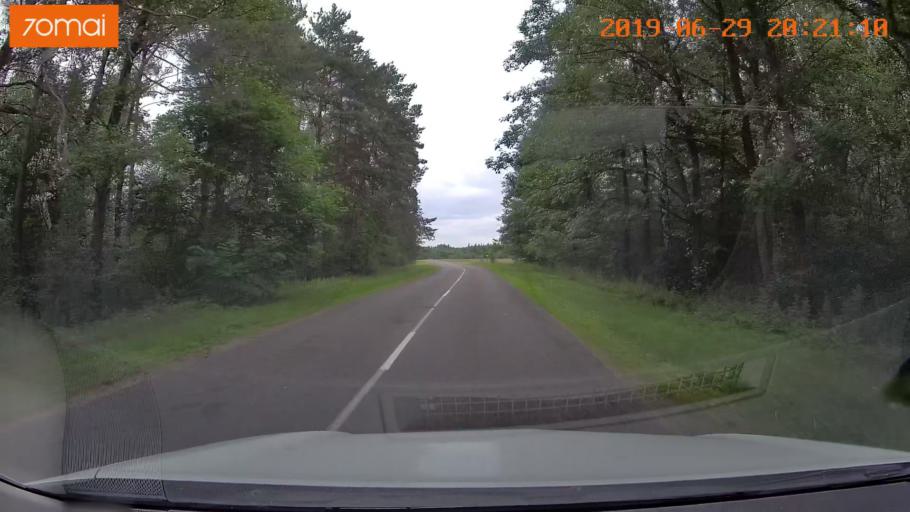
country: BY
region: Brest
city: Asnyezhytsy
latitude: 52.4169
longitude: 26.2523
